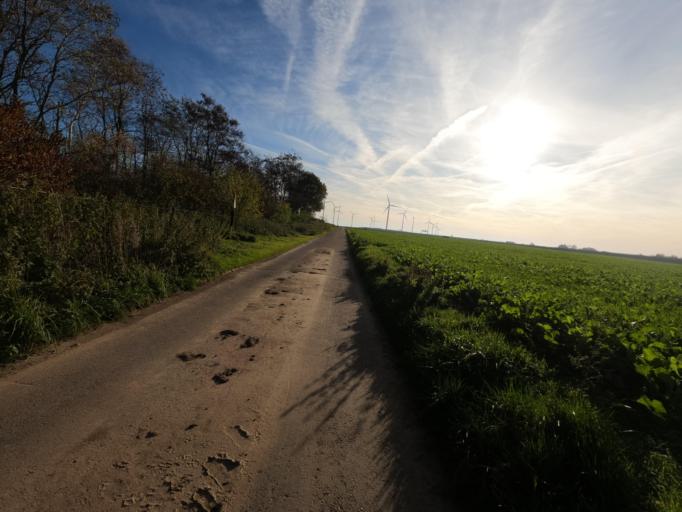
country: DE
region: North Rhine-Westphalia
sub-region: Regierungsbezirk Koln
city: Titz
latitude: 51.0391
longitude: 6.4686
